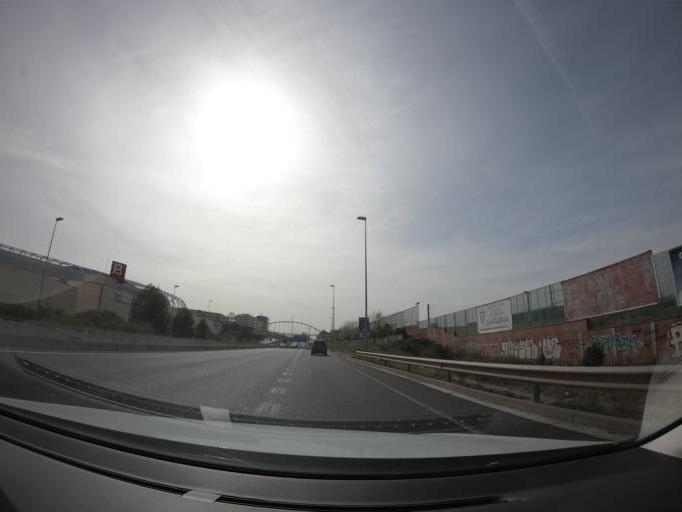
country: ES
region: La Rioja
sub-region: Provincia de La Rioja
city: Logrono
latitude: 42.4639
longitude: -2.4210
